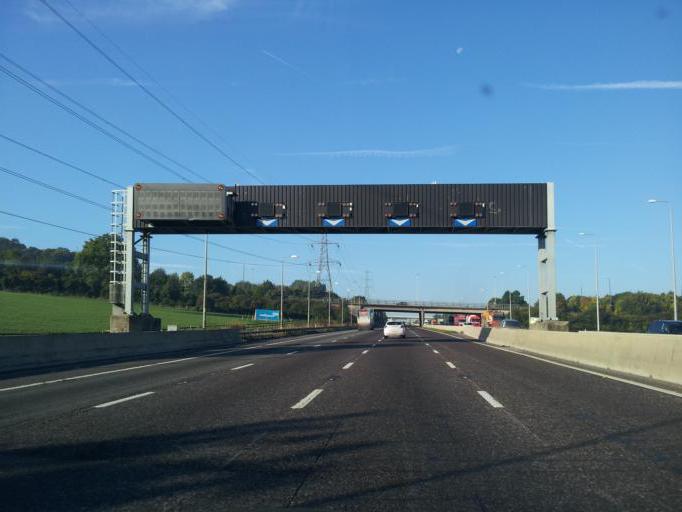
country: GB
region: England
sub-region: Calderdale
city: Brighouse
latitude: 53.6836
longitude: -1.7779
